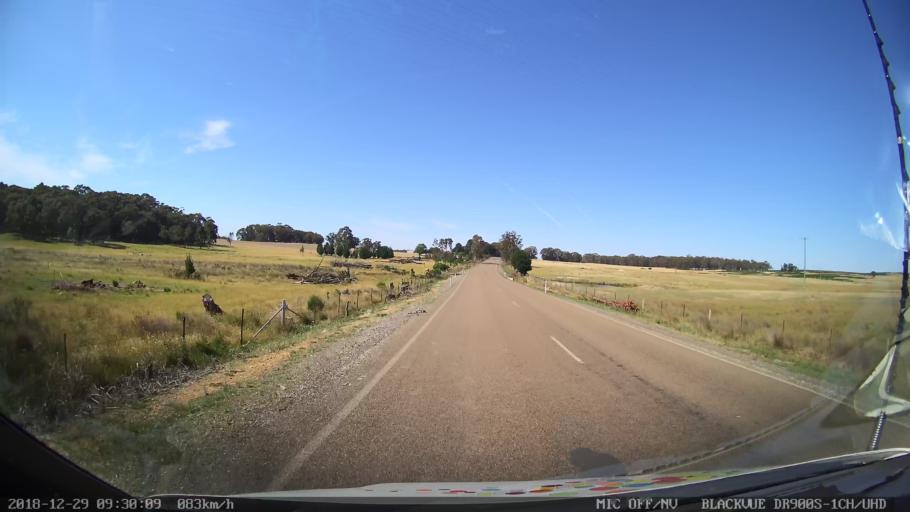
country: AU
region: New South Wales
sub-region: Upper Lachlan Shire
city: Crookwell
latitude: -34.5957
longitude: 149.3710
